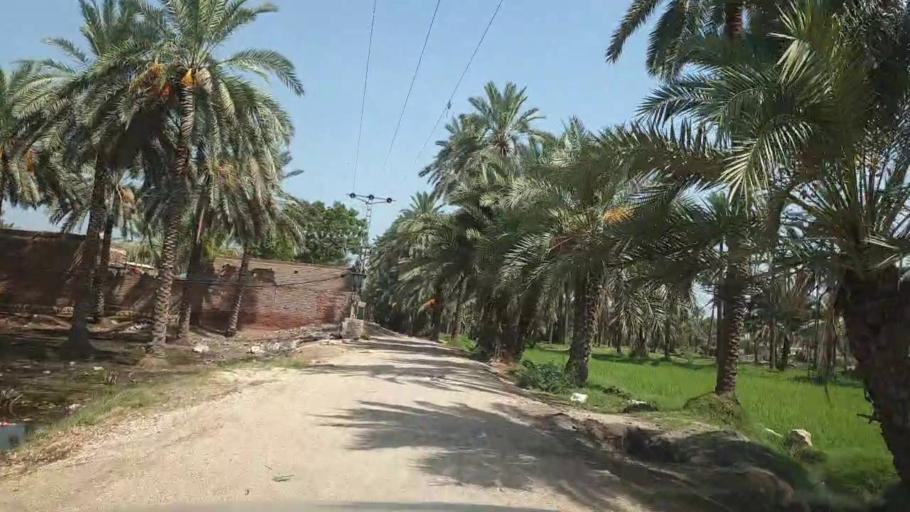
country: PK
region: Sindh
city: Rohri
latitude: 27.6931
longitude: 68.9477
